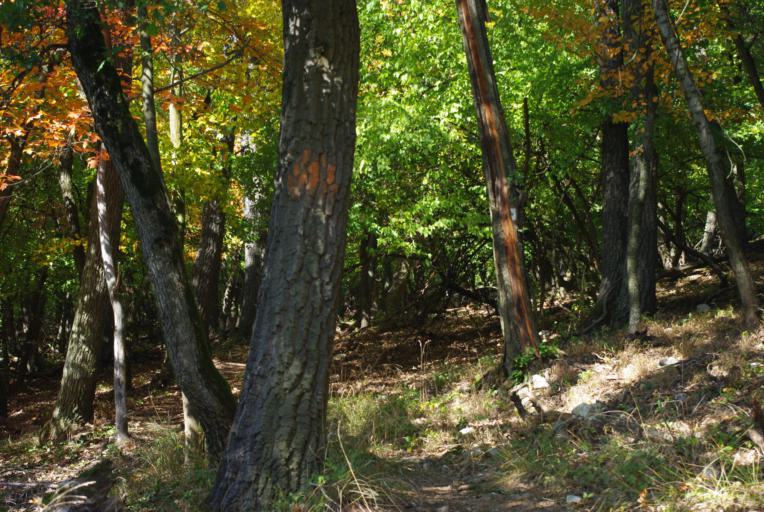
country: HU
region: Pest
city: Budakeszi
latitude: 47.5328
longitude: 18.9117
